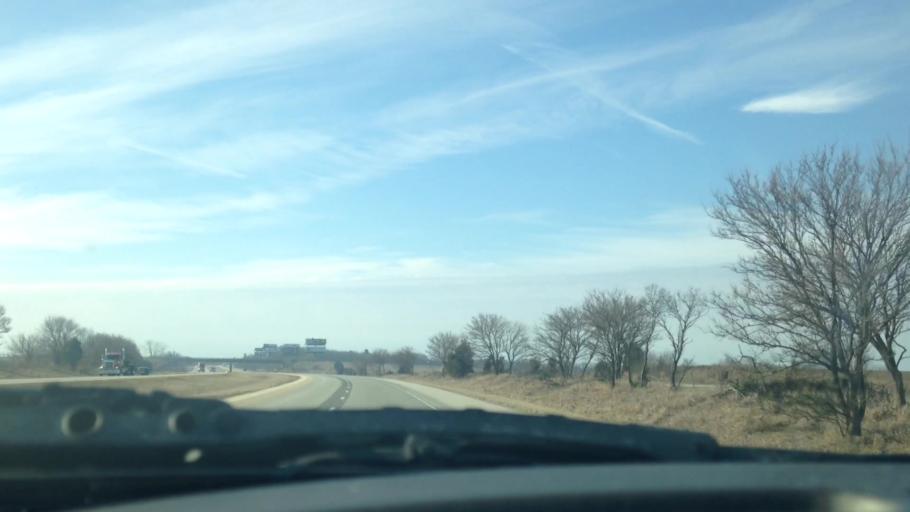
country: US
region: Illinois
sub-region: Ford County
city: Paxton
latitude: 40.5221
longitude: -88.0844
